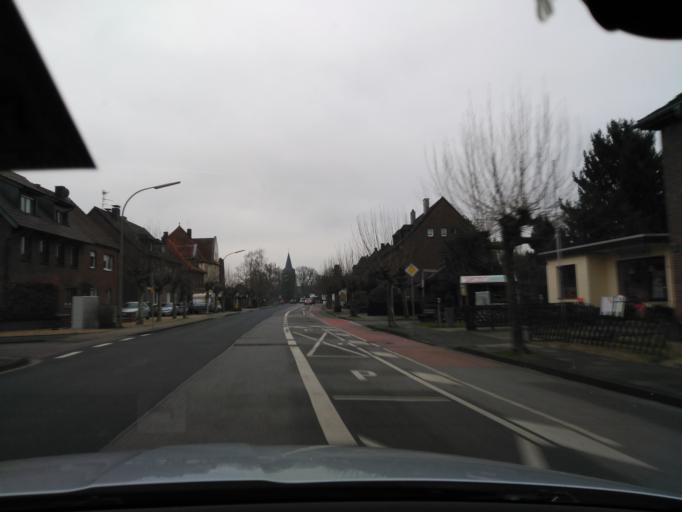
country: DE
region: North Rhine-Westphalia
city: Wegberg
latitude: 51.1351
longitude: 6.3007
